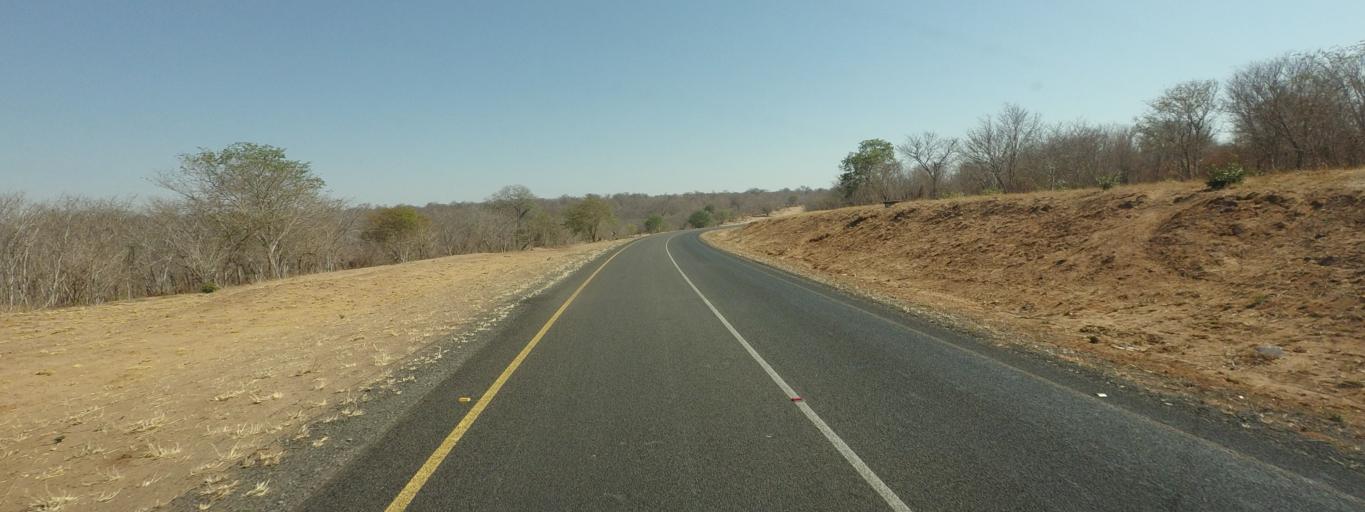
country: BW
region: North West
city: Kasane
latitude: -17.8796
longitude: 25.2127
